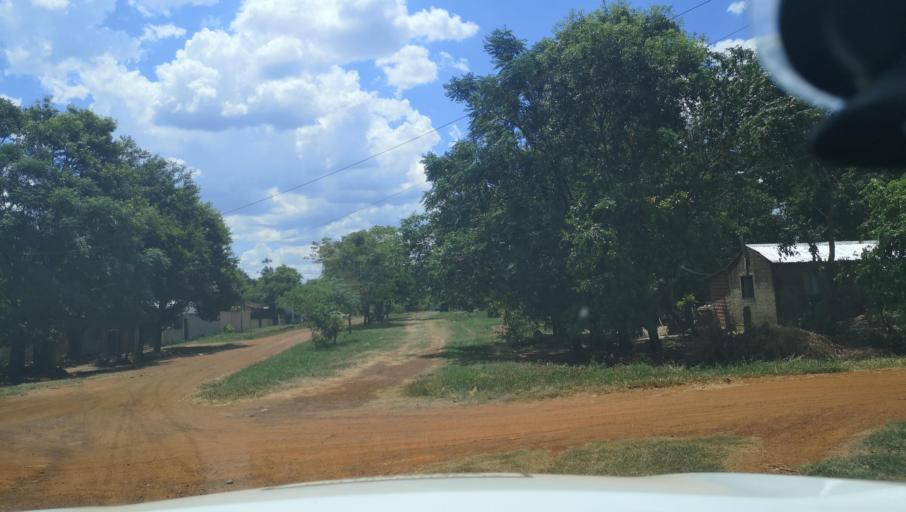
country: PY
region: Itapua
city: Carmen del Parana
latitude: -27.1701
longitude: -56.2414
